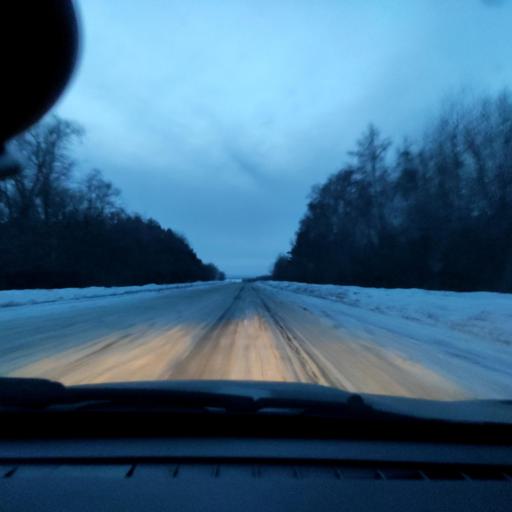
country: RU
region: Samara
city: Tol'yatti
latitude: 53.4963
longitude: 49.2805
